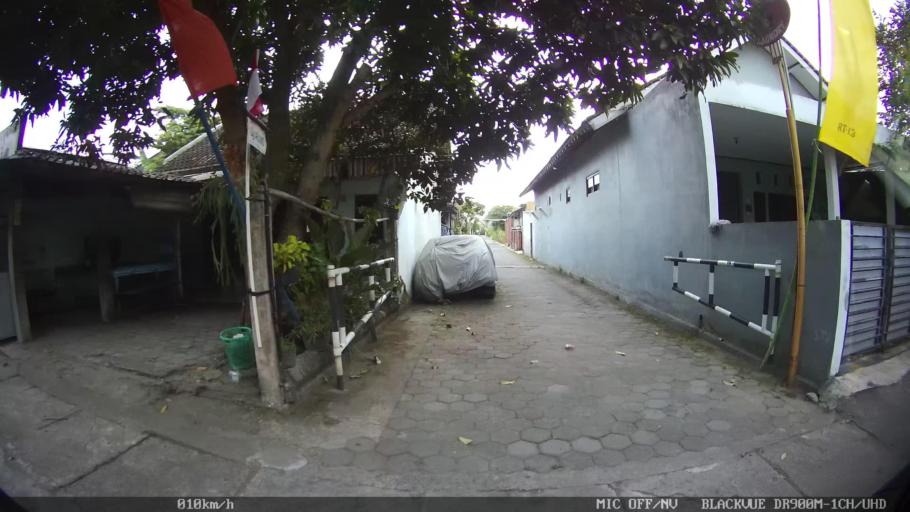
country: ID
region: Daerah Istimewa Yogyakarta
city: Yogyakarta
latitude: -7.8145
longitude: 110.4062
